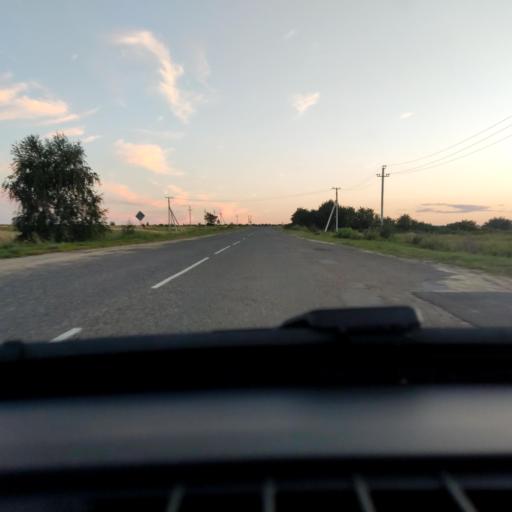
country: RU
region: Lipetsk
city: Zadonsk
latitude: 52.3137
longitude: 38.9164
